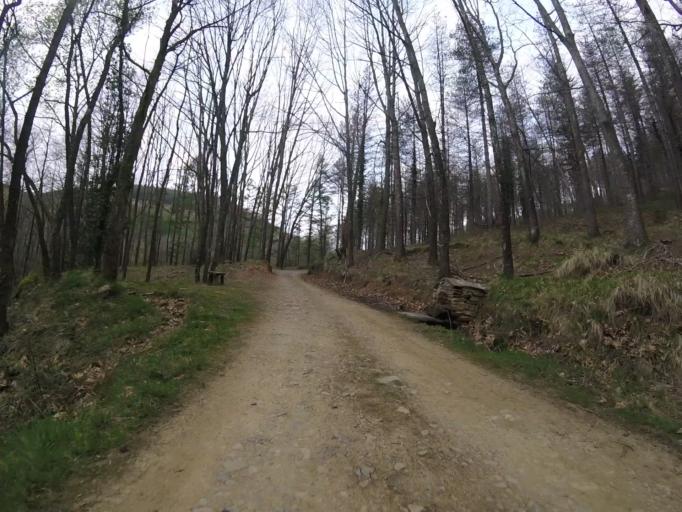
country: ES
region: Navarre
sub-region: Provincia de Navarra
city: Areso
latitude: 43.1073
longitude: -1.9454
